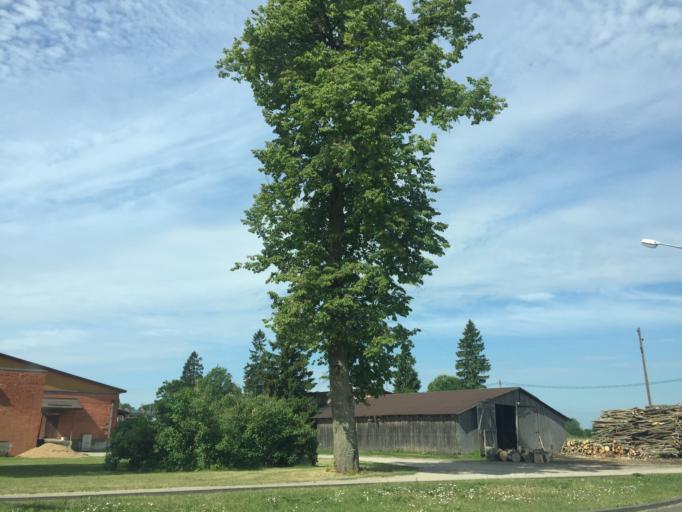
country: LV
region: Pargaujas
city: Stalbe
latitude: 57.3559
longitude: 24.9516
